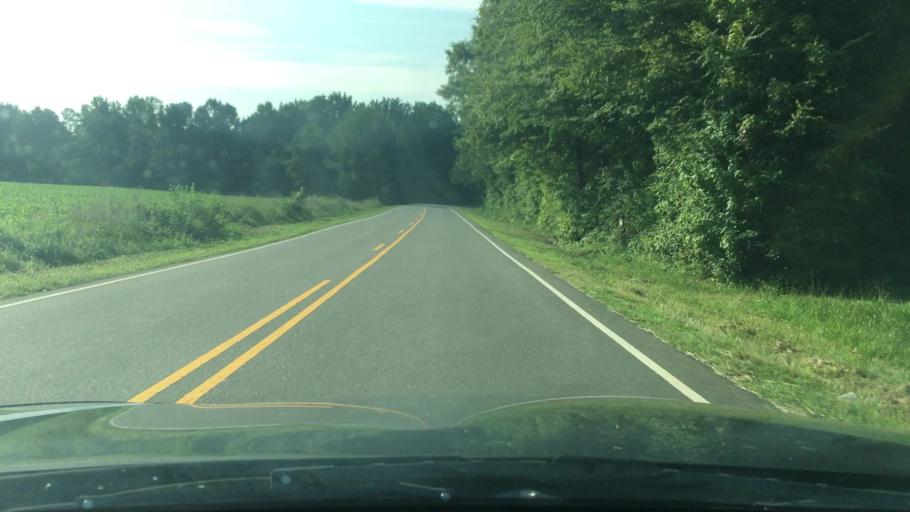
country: US
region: North Carolina
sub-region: Alamance County
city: Green Level
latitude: 36.2624
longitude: -79.3390
